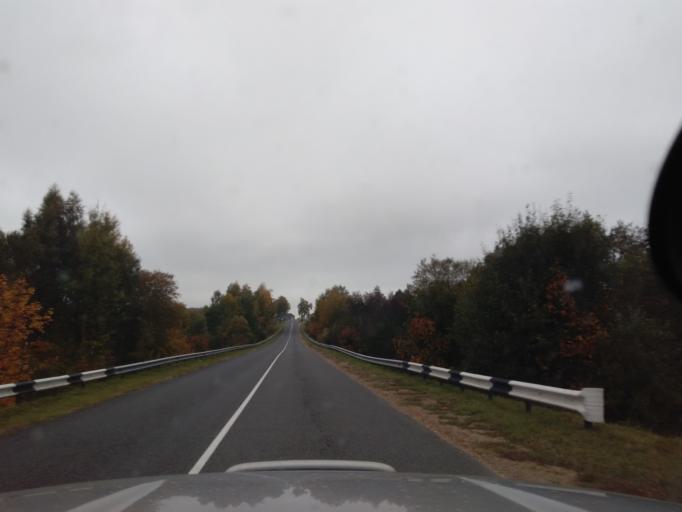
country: BY
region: Minsk
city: Kapyl'
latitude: 53.1501
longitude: 27.2041
